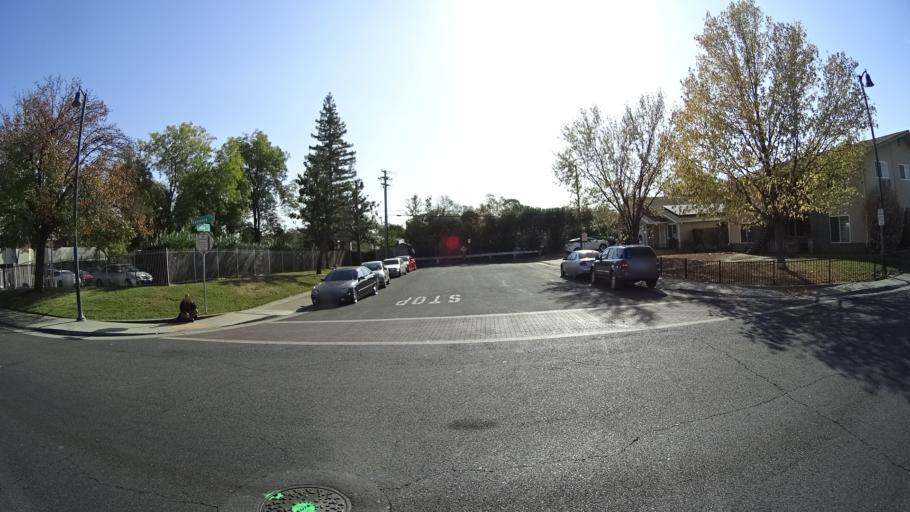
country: US
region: California
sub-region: Sacramento County
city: Citrus Heights
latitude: 38.6853
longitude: -121.2727
